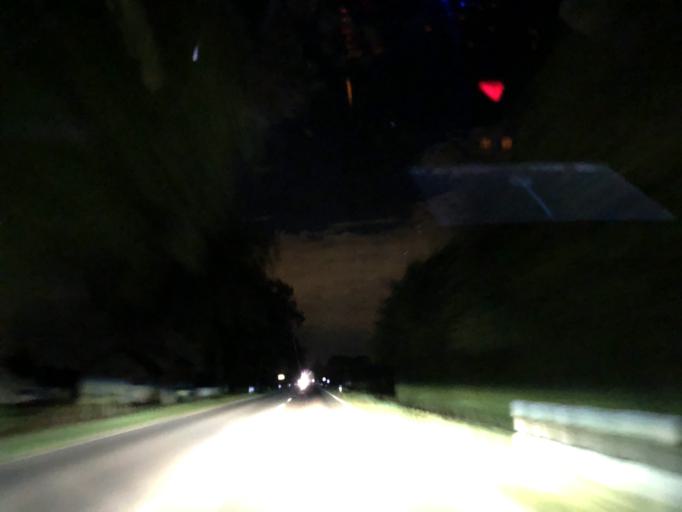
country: DE
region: Bavaria
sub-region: Upper Bavaria
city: Moosinning
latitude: 48.2481
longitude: 11.8336
